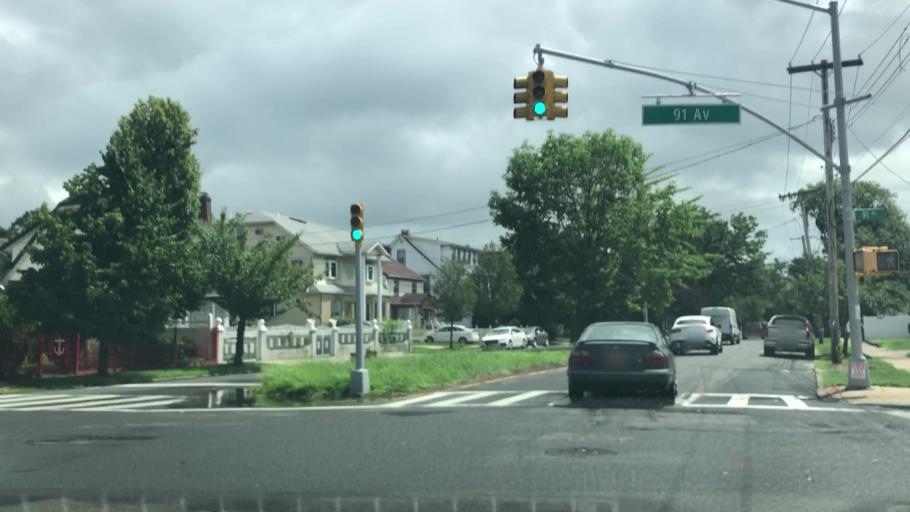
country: US
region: New York
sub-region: Nassau County
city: Bellerose Terrace
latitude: 40.7201
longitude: -73.7500
